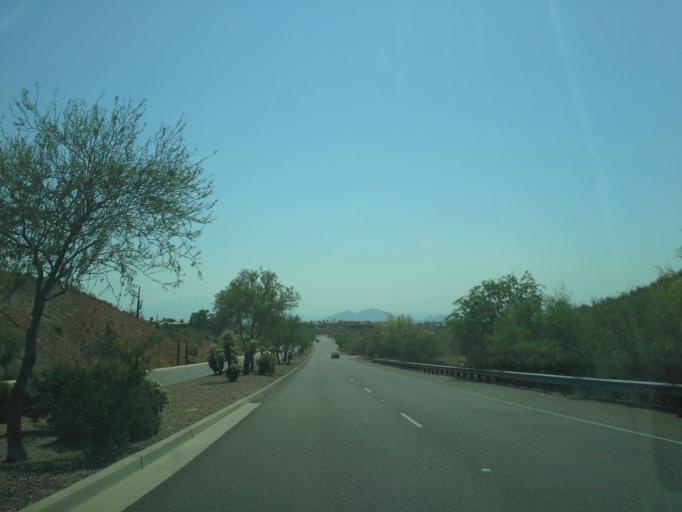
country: US
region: Arizona
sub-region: Maricopa County
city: Fountain Hills
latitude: 33.5814
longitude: -111.7462
